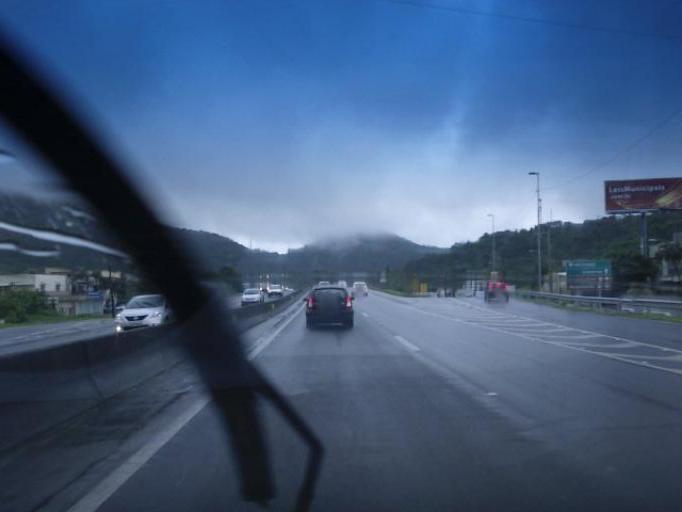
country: BR
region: Santa Catarina
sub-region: Itapema
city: Itapema
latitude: -27.0630
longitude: -48.5960
